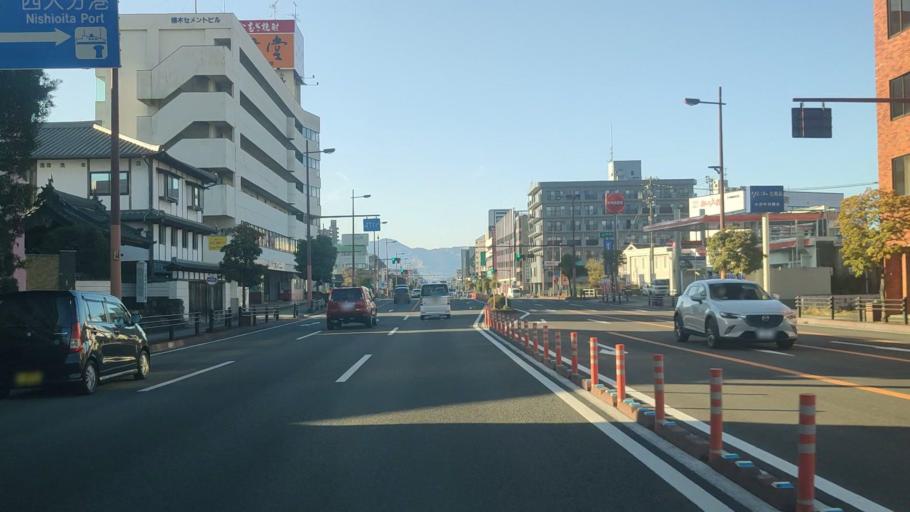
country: JP
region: Oita
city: Oita
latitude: 33.2430
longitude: 131.5894
